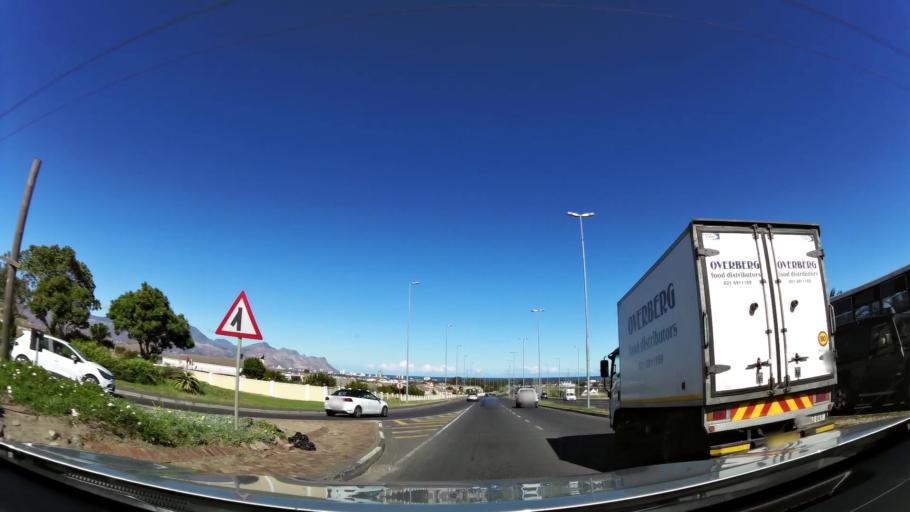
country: ZA
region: Western Cape
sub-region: Cape Winelands District Municipality
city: Stellenbosch
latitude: -34.0696
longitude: 18.8254
